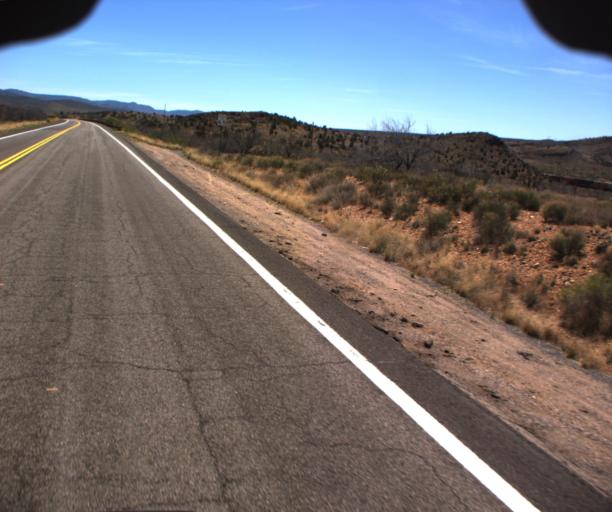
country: US
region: Arizona
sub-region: Mohave County
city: New Kingman-Butler
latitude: 35.3710
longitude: -113.7179
